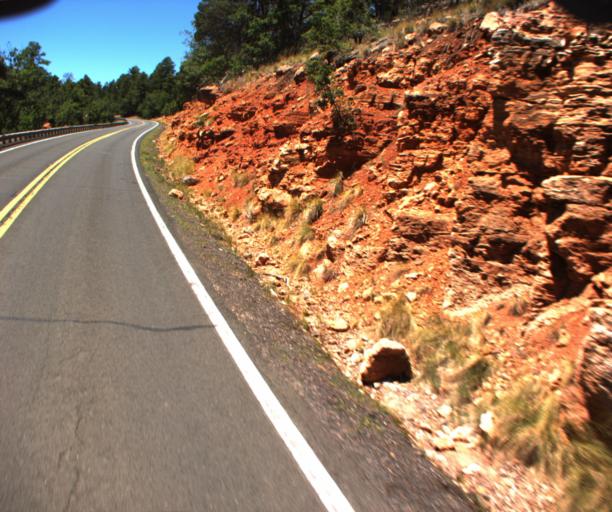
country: US
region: Arizona
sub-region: Gila County
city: Pine
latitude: 34.5949
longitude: -111.2460
